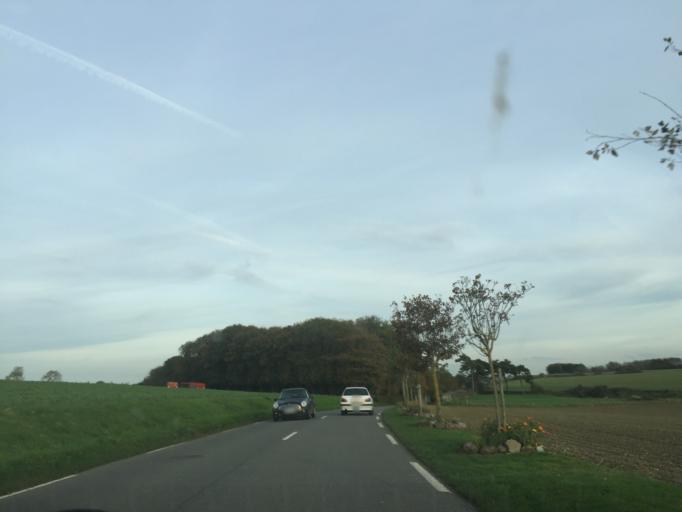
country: FR
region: Nord-Pas-de-Calais
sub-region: Departement du Pas-de-Calais
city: Coquelles
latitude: 50.9156
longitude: 1.7794
